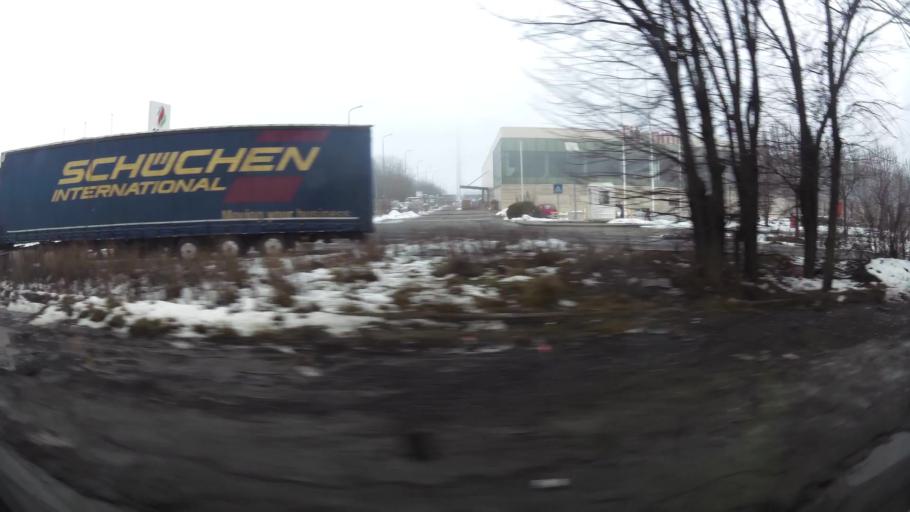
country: RO
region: Ilfov
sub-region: Comuna Chiajna
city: Chiajna
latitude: 44.4344
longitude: 25.9672
